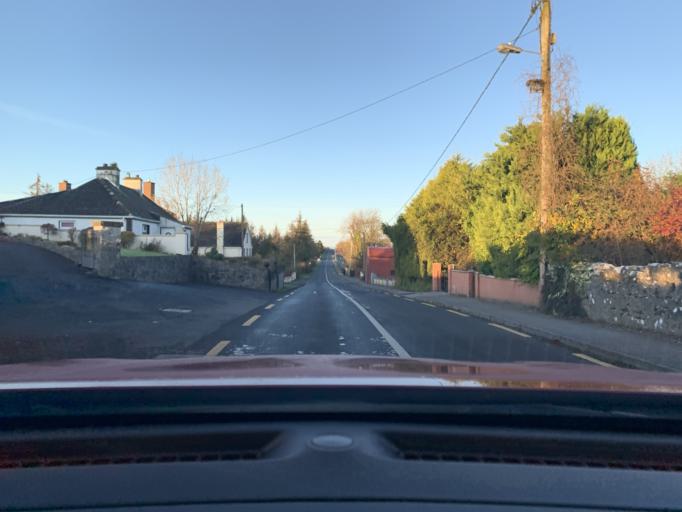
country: IE
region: Connaught
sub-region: Sligo
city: Ballymote
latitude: 54.0872
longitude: -8.5267
